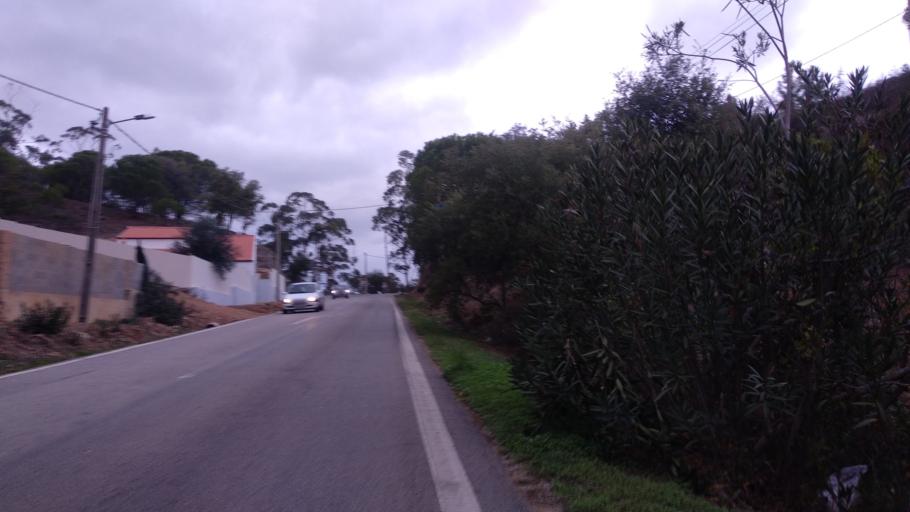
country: PT
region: Faro
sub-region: Sao Bras de Alportel
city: Sao Bras de Alportel
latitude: 37.1788
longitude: -7.9102
